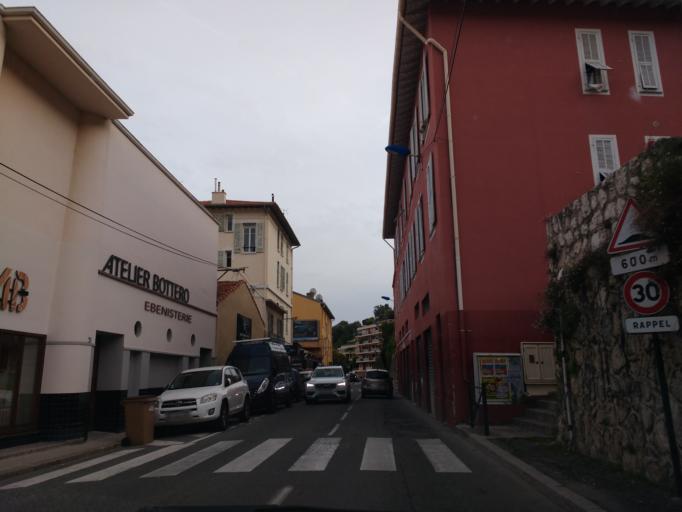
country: FR
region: Provence-Alpes-Cote d'Azur
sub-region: Departement des Alpes-Maritimes
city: Beaulieu-sur-Mer
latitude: 43.7053
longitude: 7.3269
